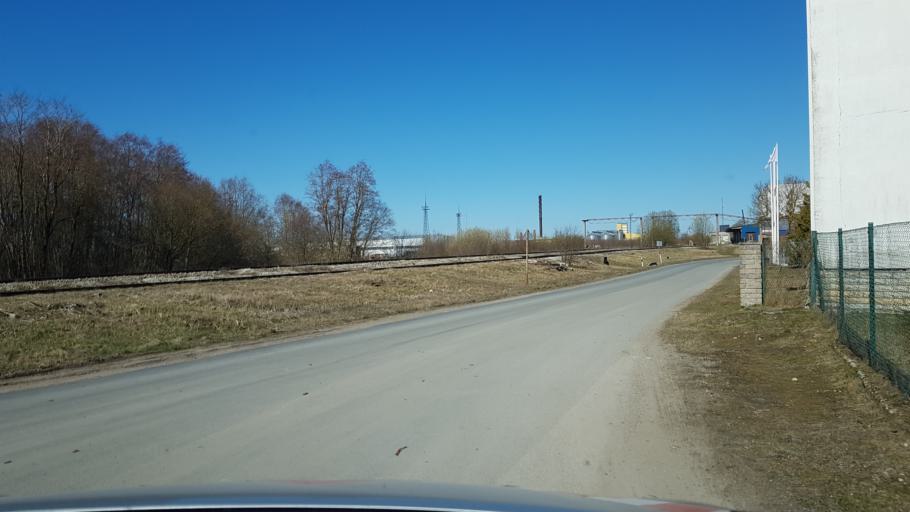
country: EE
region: Laeaene-Virumaa
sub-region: Someru vald
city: Someru
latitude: 59.3631
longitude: 26.3955
